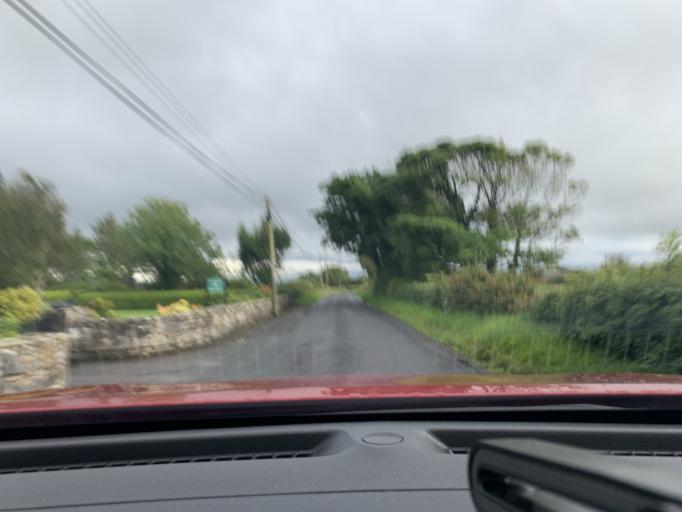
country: IE
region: Connaught
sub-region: Sligo
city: Strandhill
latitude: 54.3585
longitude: -8.5414
